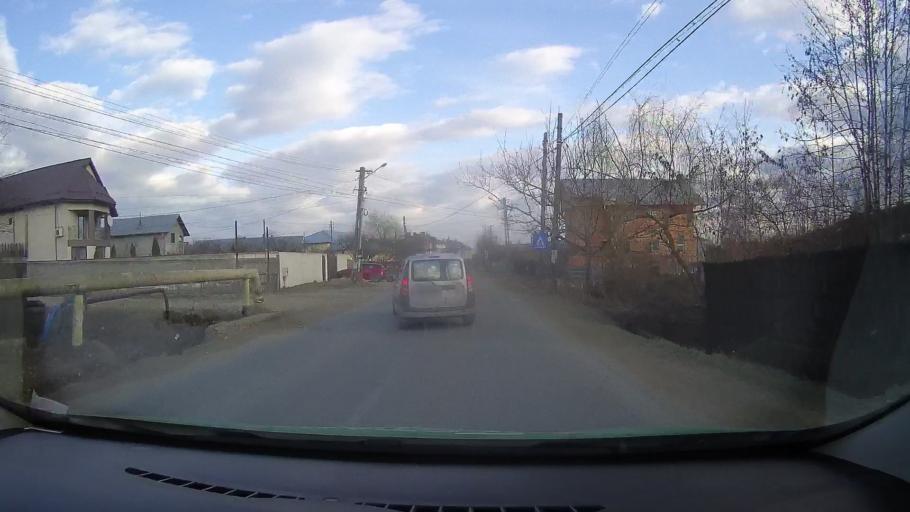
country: RO
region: Dambovita
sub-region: Comuna Gura Ocnitei
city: Gura Ocnitei
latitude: 44.9460
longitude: 25.5598
